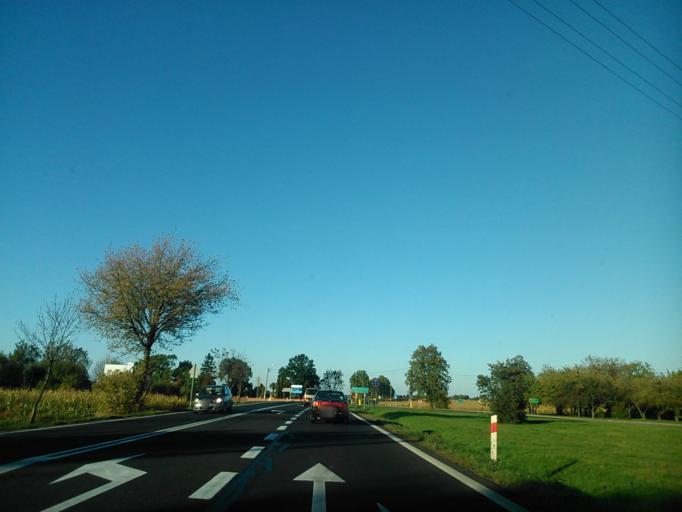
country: PL
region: Kujawsko-Pomorskie
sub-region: Powiat golubsko-dobrzynski
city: Kowalewo Pomorskie
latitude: 53.1197
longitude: 18.8327
